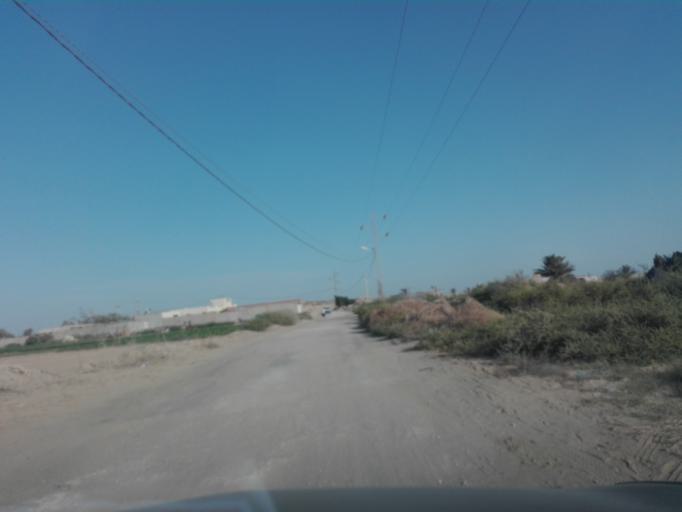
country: TN
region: Qabis
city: Gabes
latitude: 33.9593
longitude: 10.0618
